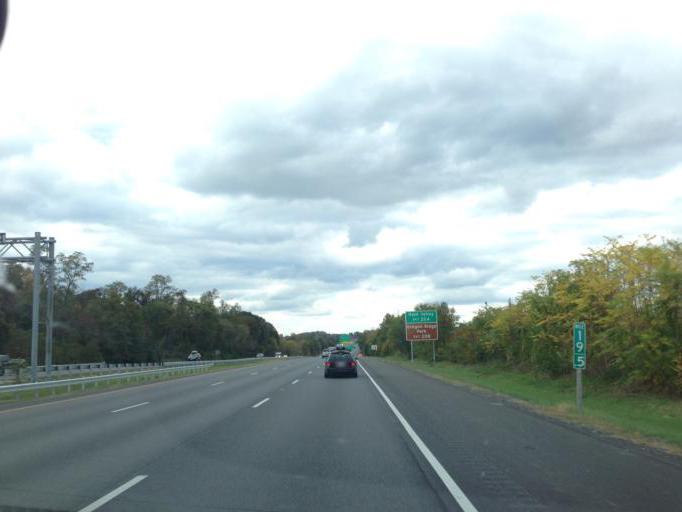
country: US
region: Maryland
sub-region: Baltimore County
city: Cockeysville
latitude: 39.4823
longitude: -76.6650
